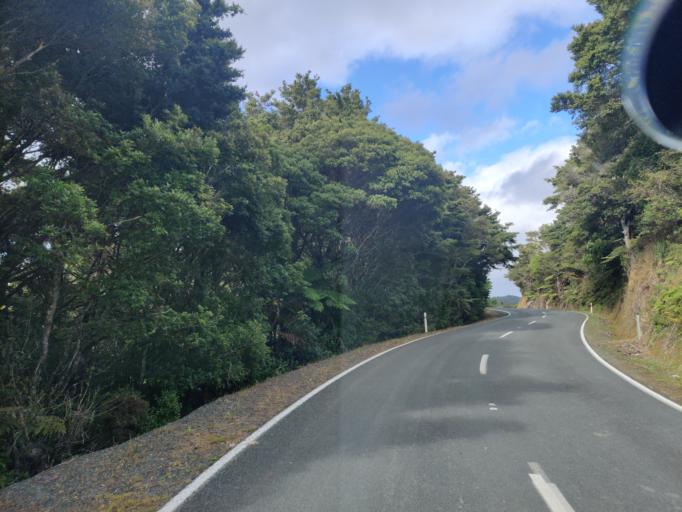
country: NZ
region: Northland
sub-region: Whangarei
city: Ngunguru
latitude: -35.5842
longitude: 174.4276
